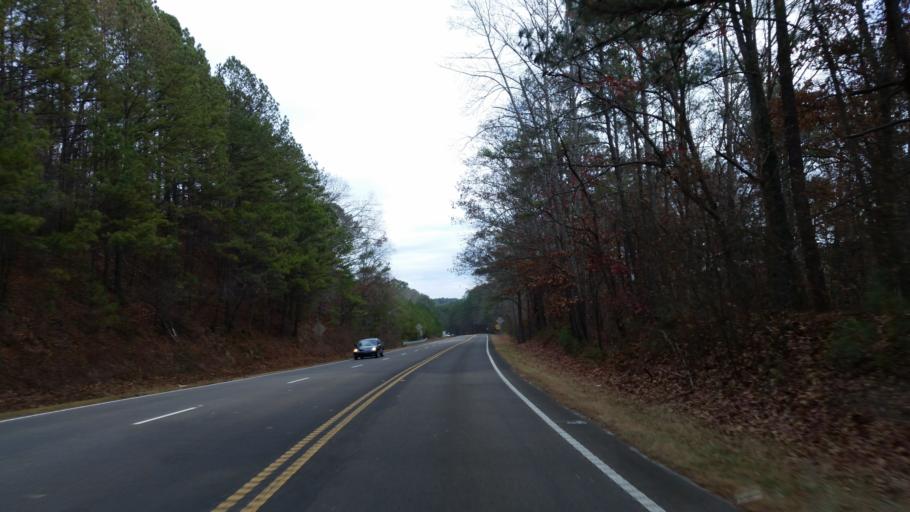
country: US
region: Georgia
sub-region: Cherokee County
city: Holly Springs
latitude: 34.2177
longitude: -84.5745
